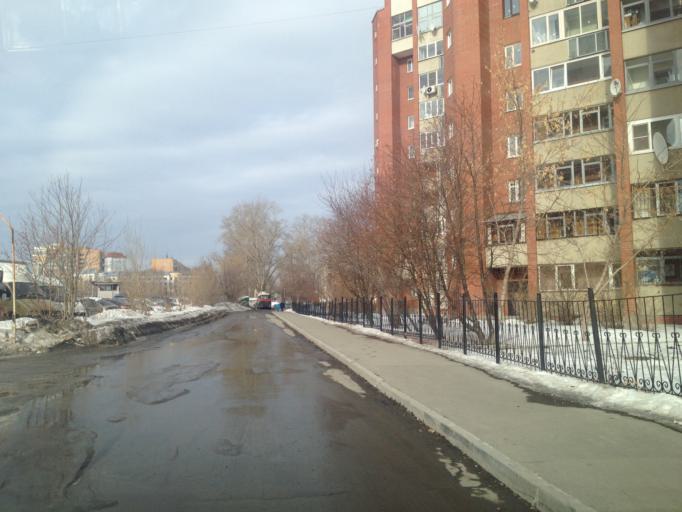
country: RU
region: Sverdlovsk
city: Yekaterinburg
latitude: 56.8485
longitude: 60.5962
